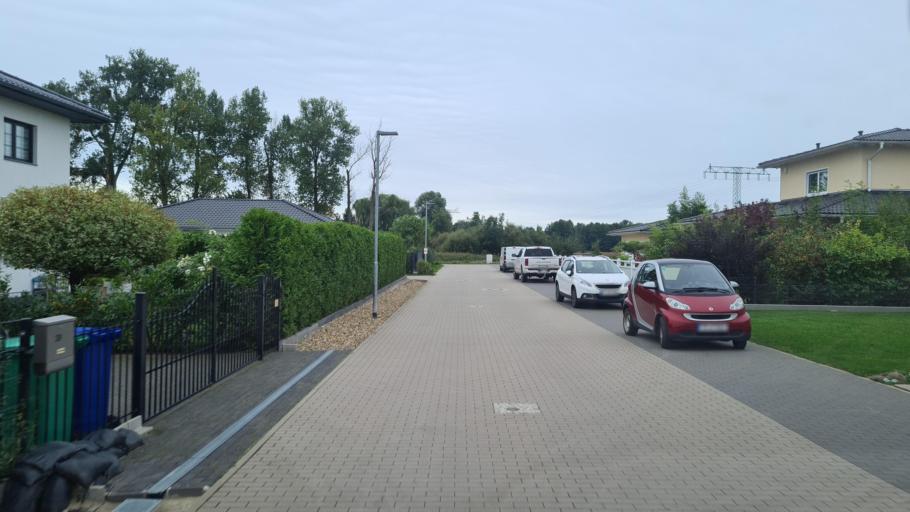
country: DE
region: Brandenburg
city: Zossen
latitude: 52.2026
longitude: 13.4545
